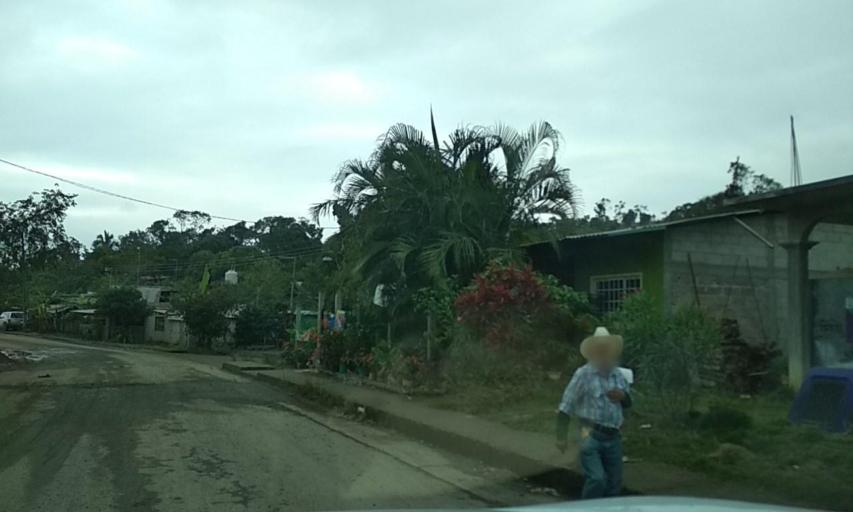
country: MX
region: Veracruz
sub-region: Coatzintla
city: Manuel Maria Contreras
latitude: 20.3622
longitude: -97.5133
